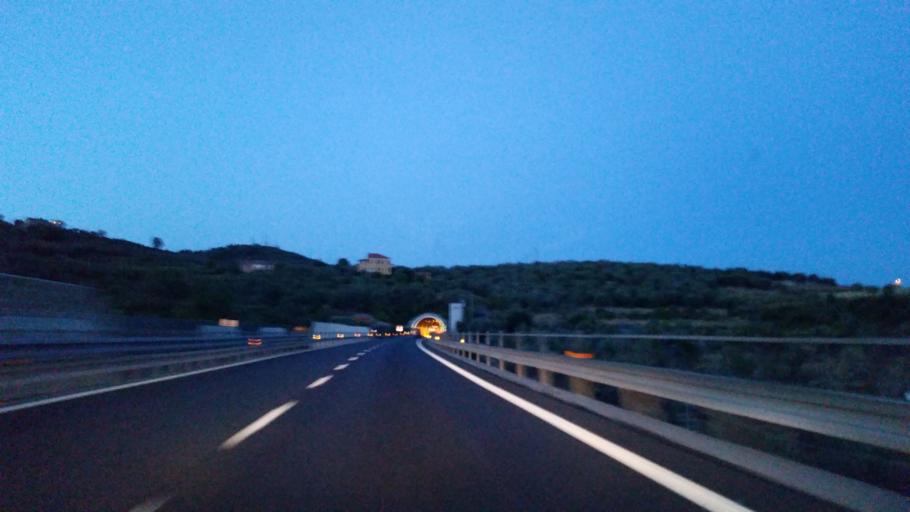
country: IT
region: Liguria
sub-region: Provincia di Imperia
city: Imperia
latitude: 43.8862
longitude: 8.0109
